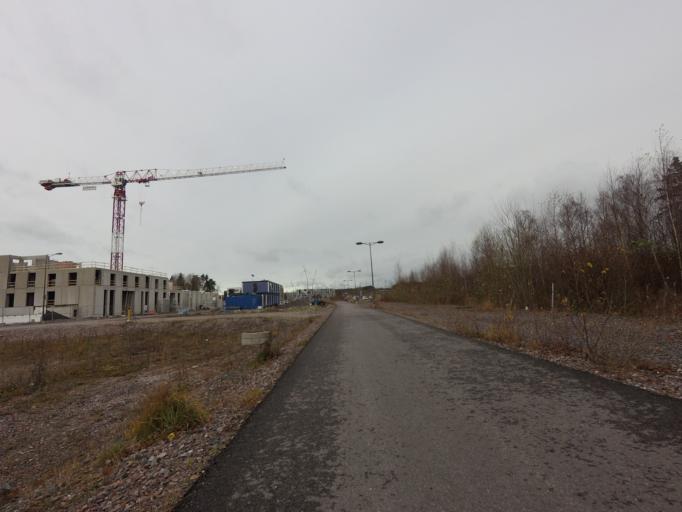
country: FI
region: Uusimaa
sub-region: Helsinki
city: Kauniainen
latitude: 60.1860
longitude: 24.7440
